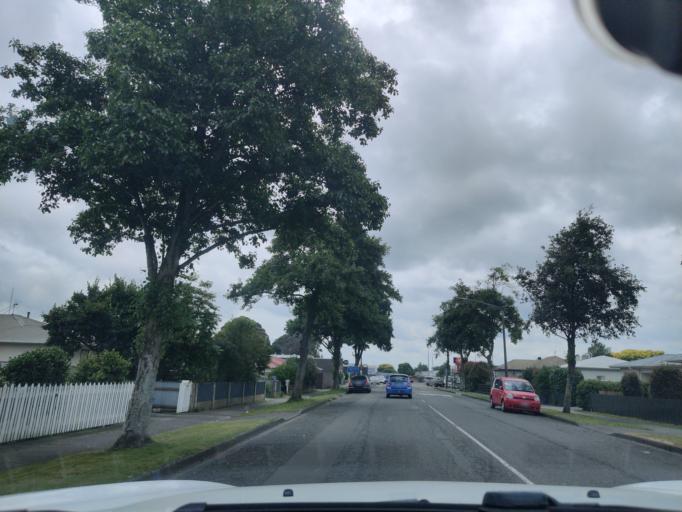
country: NZ
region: Manawatu-Wanganui
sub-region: Palmerston North City
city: Palmerston North
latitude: -40.3521
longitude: 175.5856
